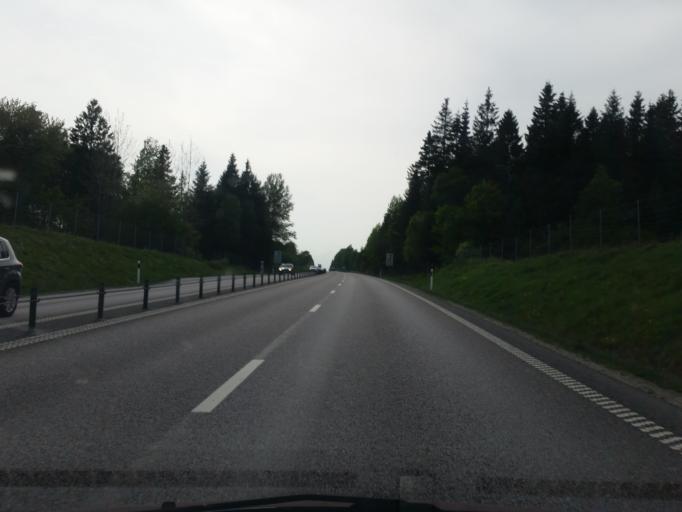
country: SE
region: Vaestra Goetaland
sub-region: Ulricehamns Kommun
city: Ulricehamn
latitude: 57.7969
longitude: 13.5795
